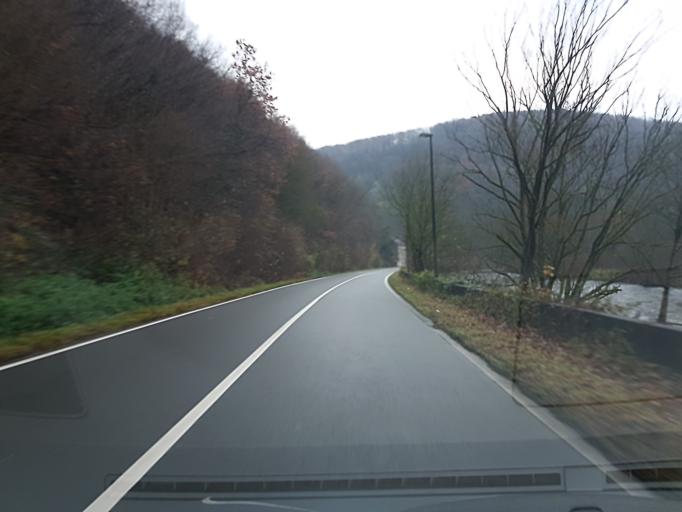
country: BE
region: Wallonia
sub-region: Province de Liege
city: Olne
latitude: 50.5748
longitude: 5.7638
